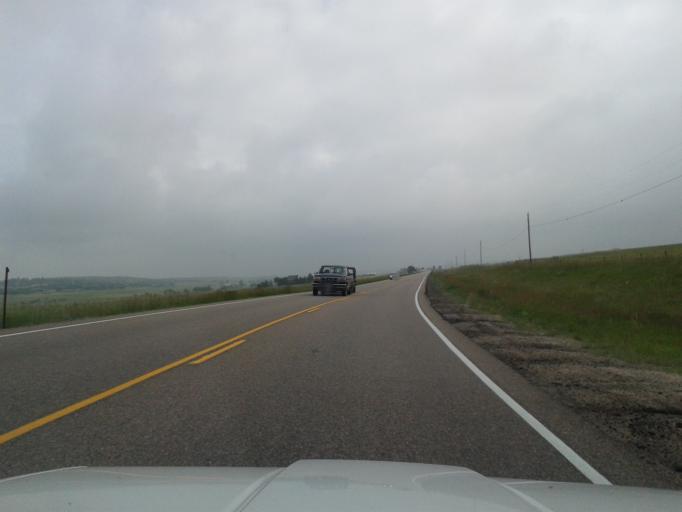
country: US
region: Colorado
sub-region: El Paso County
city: Woodmoor
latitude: 39.1893
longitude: -104.7296
